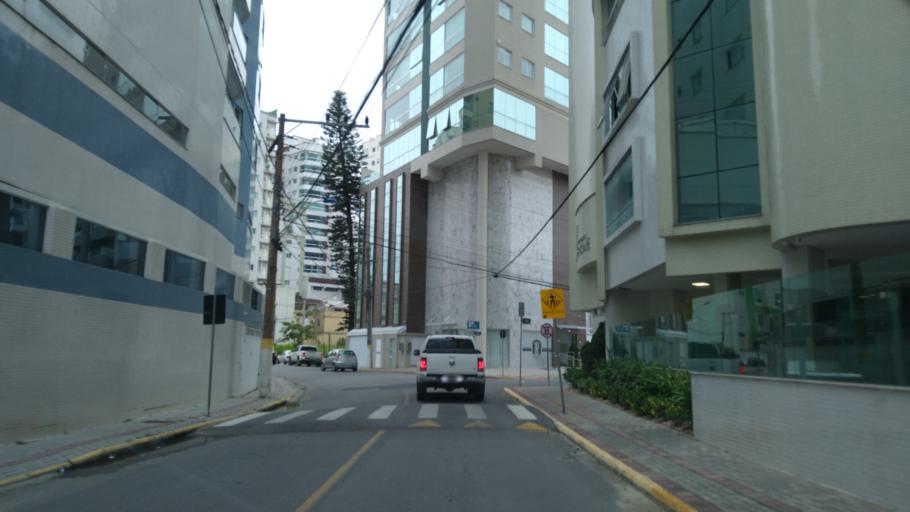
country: BR
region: Santa Catarina
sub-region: Itapema
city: Itapema
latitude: -27.0952
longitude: -48.6138
